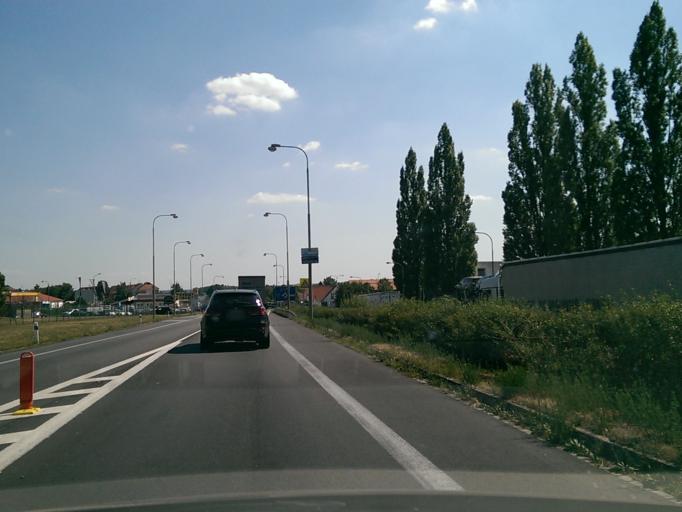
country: CZ
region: South Moravian
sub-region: Okres Breclav
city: Mikulov
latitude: 48.8084
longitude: 16.6260
